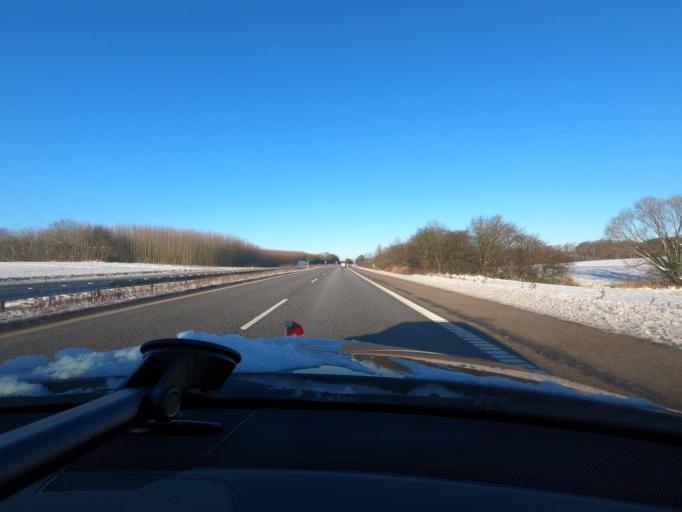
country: DK
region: South Denmark
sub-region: Aabenraa Kommune
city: Rodekro
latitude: 55.0387
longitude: 9.3539
